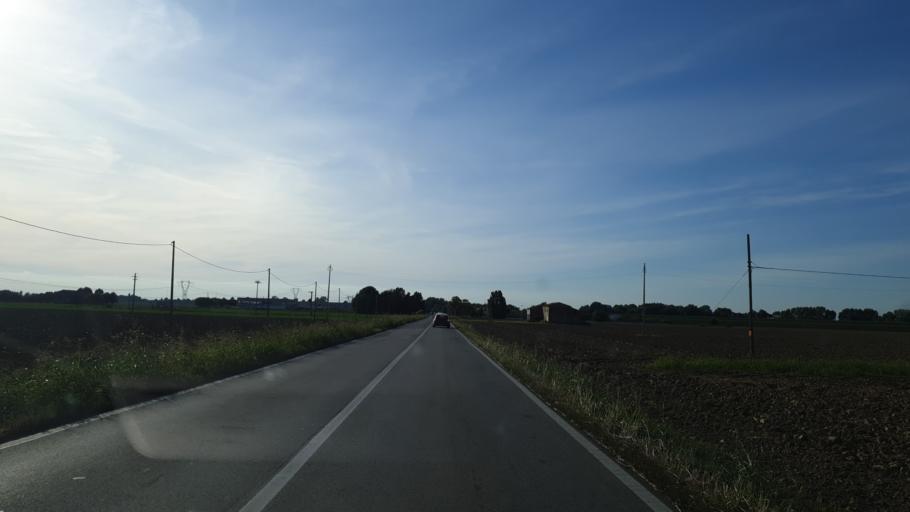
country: IT
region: Emilia-Romagna
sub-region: Provincia di Ravenna
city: Voltana
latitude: 44.5514
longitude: 11.9498
